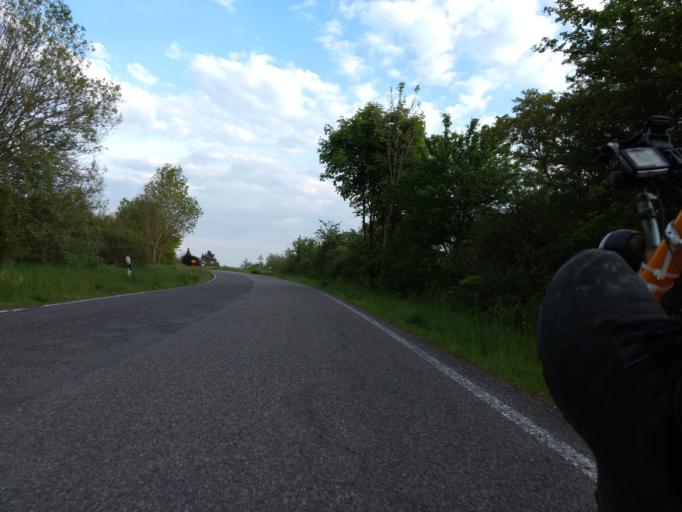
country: DE
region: Saarland
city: Beckingen
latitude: 49.3980
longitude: 6.6697
